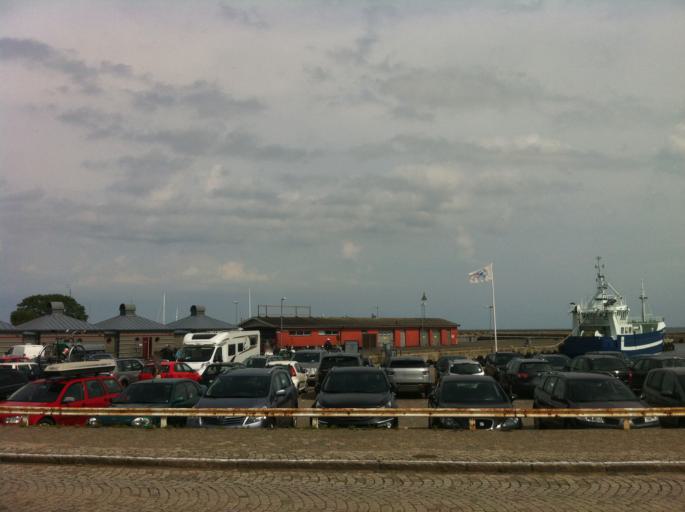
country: SE
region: Skane
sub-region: Simrishamns Kommun
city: Simrishamn
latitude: 55.5569
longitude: 14.3536
